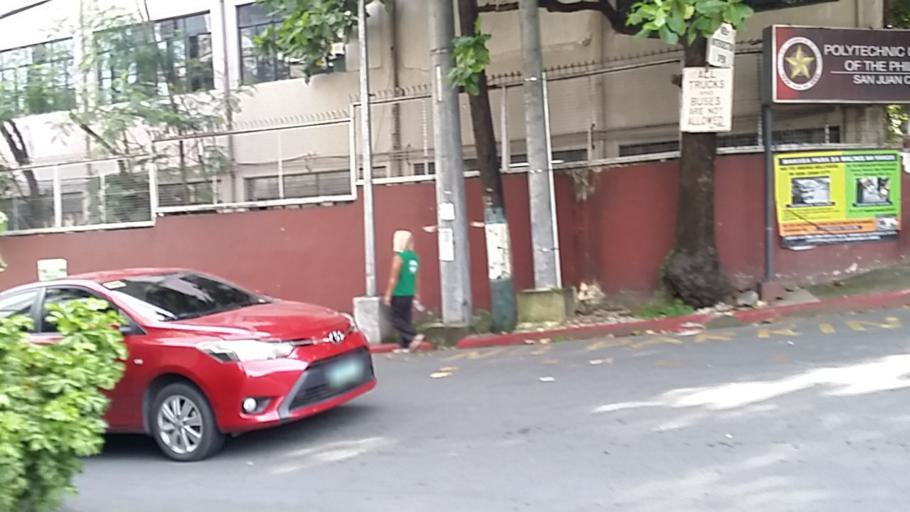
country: PH
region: Metro Manila
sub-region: San Juan
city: San Juan
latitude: 14.5939
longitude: 121.0398
